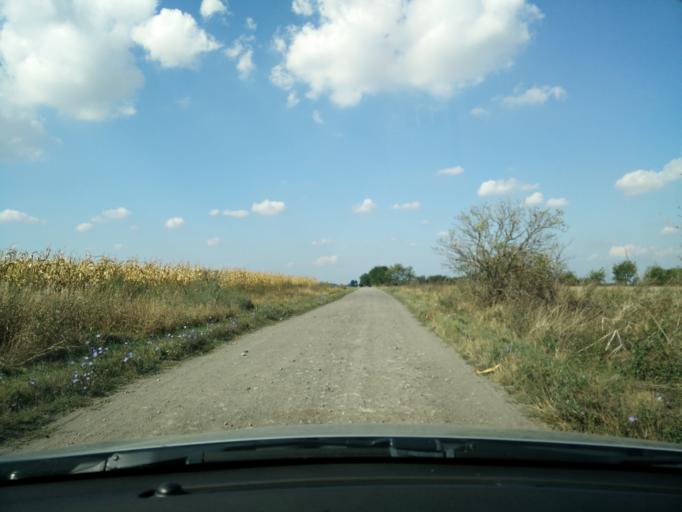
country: PL
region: Greater Poland Voivodeship
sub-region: Powiat poznanski
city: Kleszczewo
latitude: 52.2599
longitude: 17.1885
